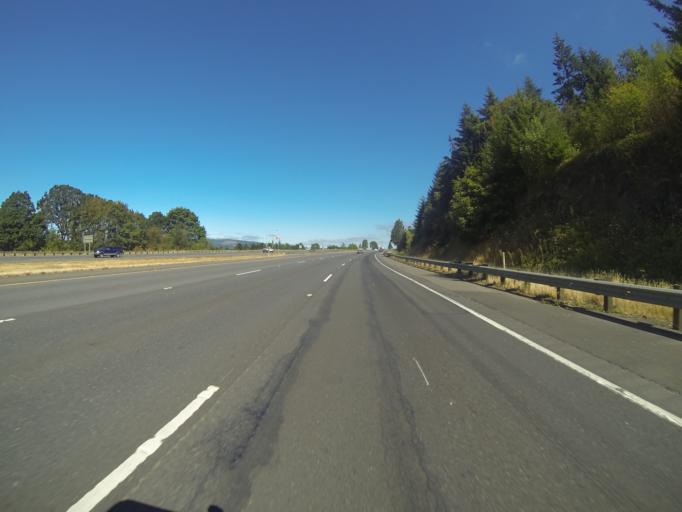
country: US
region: Washington
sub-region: Cowlitz County
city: Kalama
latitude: 46.0008
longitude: -122.8428
